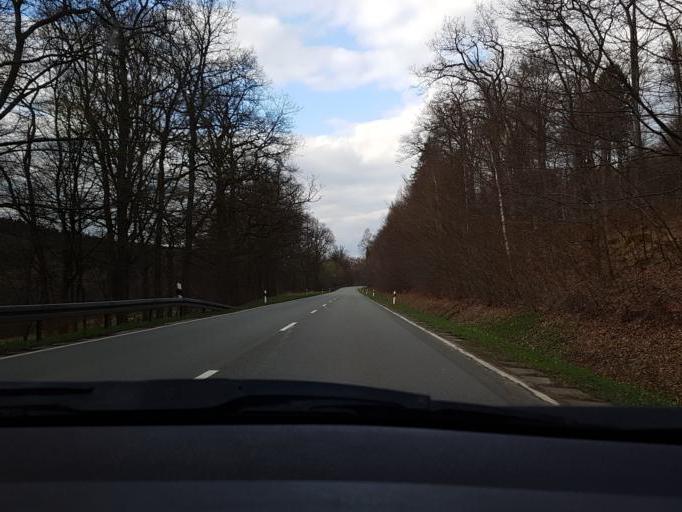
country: DE
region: Lower Saxony
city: Derental
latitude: 51.7354
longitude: 9.5135
